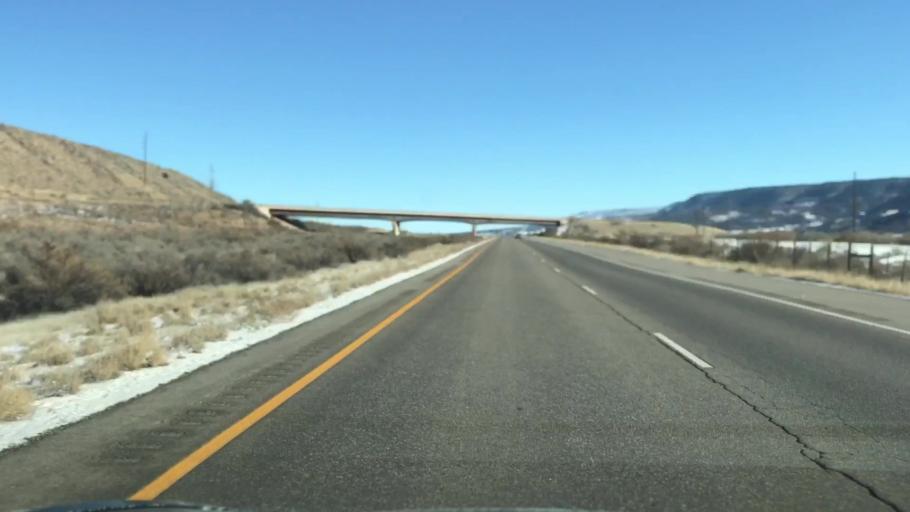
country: US
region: Colorado
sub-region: Garfield County
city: Battlement Mesa
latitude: 39.4763
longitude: -107.9963
